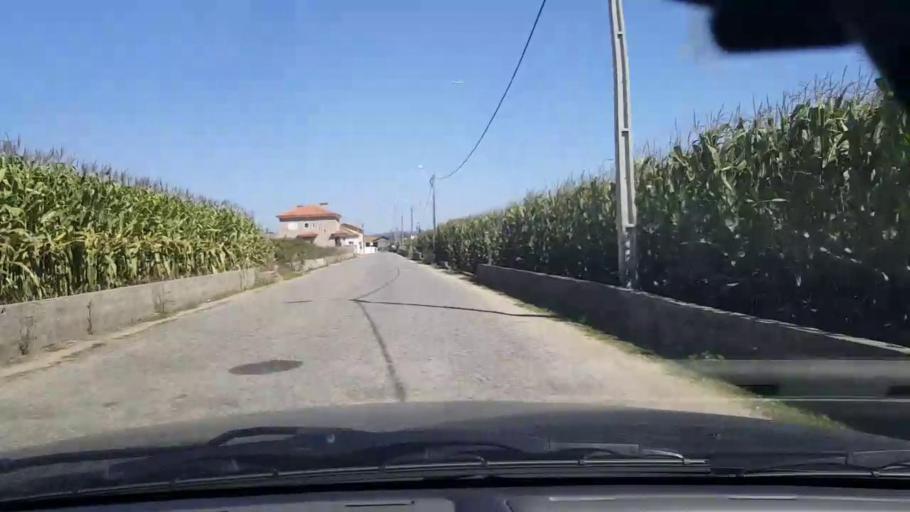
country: PT
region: Porto
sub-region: Matosinhos
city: Lavra
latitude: 41.2737
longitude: -8.7131
